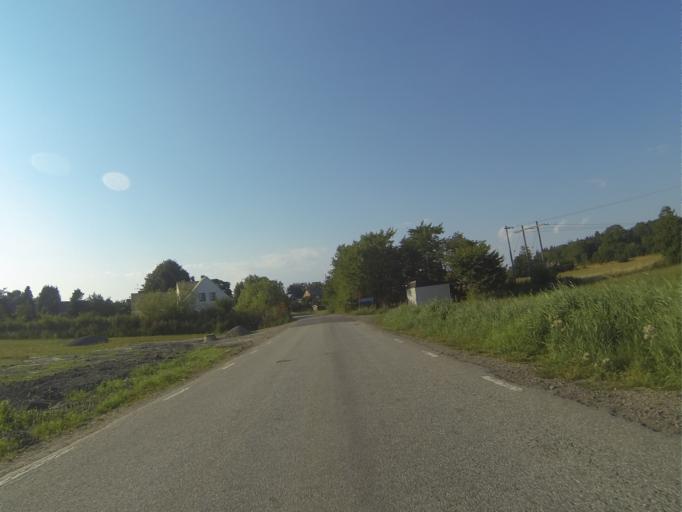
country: SE
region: Skane
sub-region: Lunds Kommun
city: Genarp
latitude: 55.6426
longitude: 13.4079
